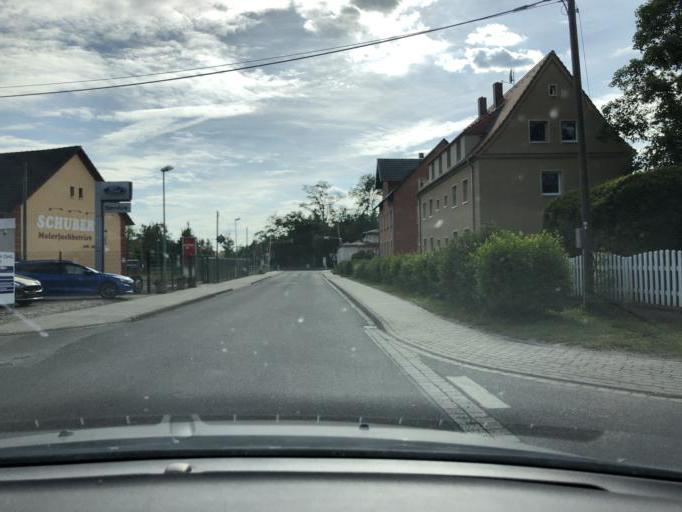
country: DE
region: Saxony
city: Brandis
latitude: 51.3248
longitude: 12.5741
